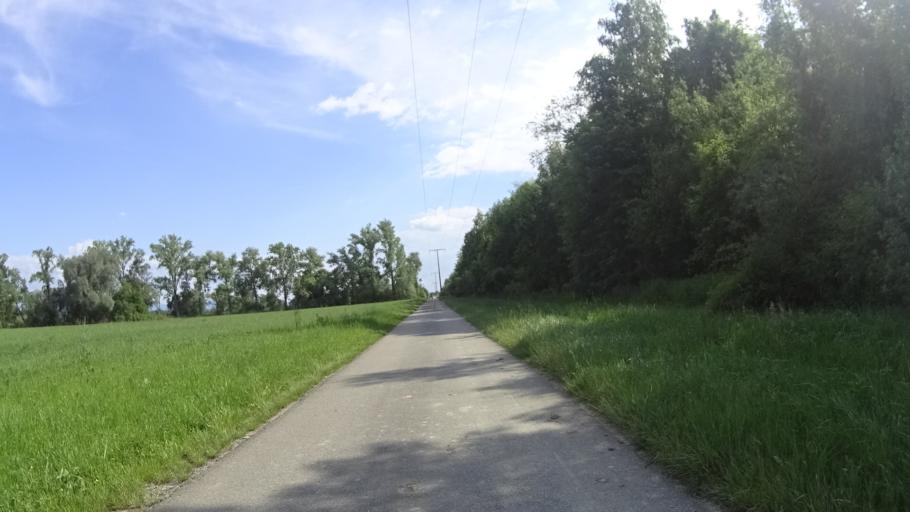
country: DE
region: Baden-Wuerttemberg
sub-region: Freiburg Region
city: Breisach am Rhein
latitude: 48.0706
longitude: 7.5908
